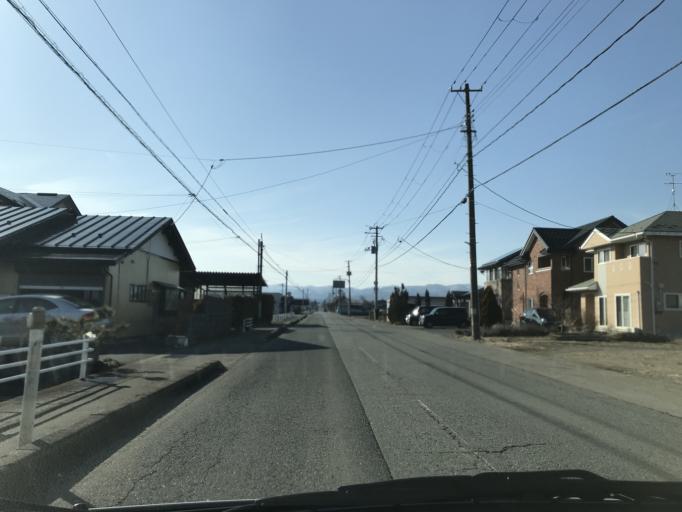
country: JP
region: Iwate
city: Kitakami
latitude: 39.2989
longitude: 141.0477
